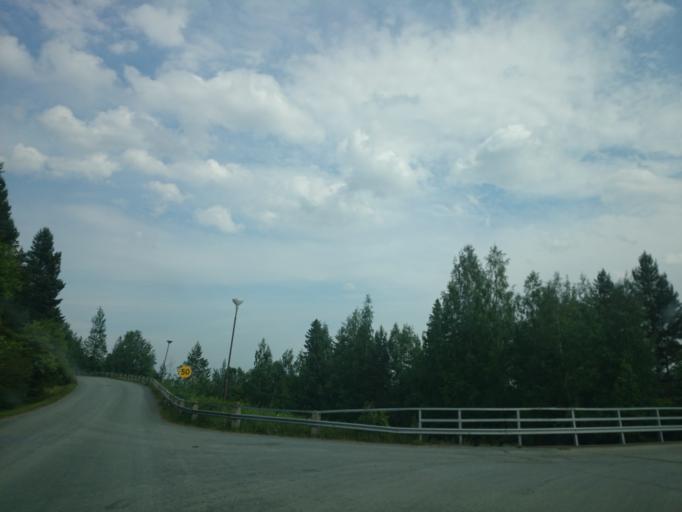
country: SE
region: Jaemtland
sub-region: Are Kommun
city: Jarpen
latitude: 63.3271
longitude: 13.3860
